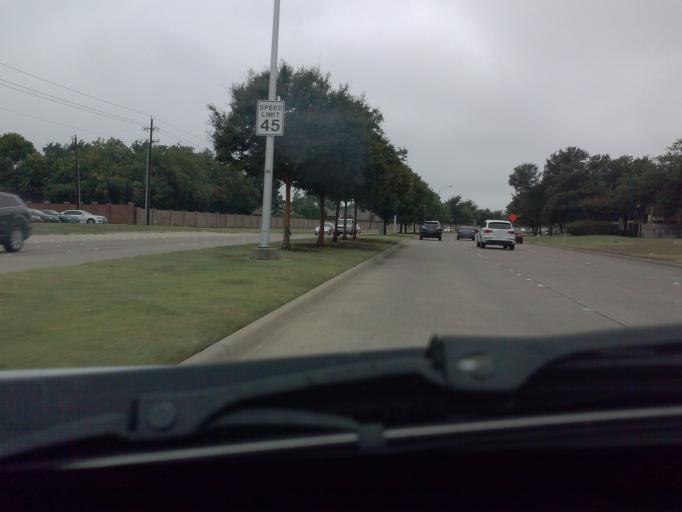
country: US
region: Texas
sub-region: Collin County
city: Plano
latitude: 33.0578
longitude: -96.7390
